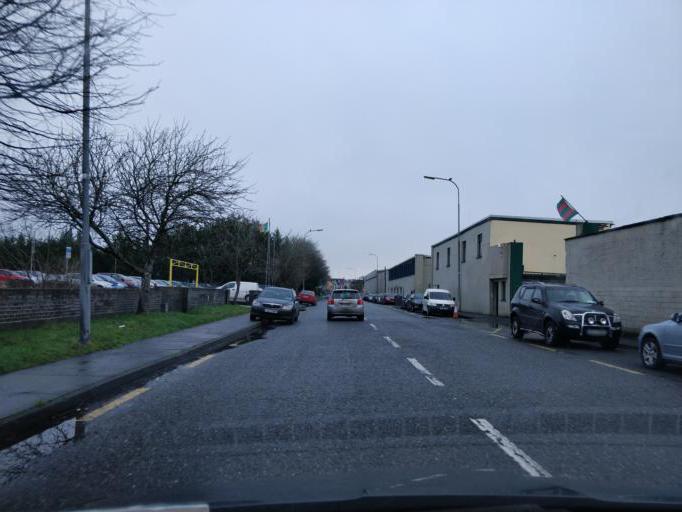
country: IE
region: Connaught
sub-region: Maigh Eo
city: Ballyhaunis
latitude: 53.7594
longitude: -8.7699
